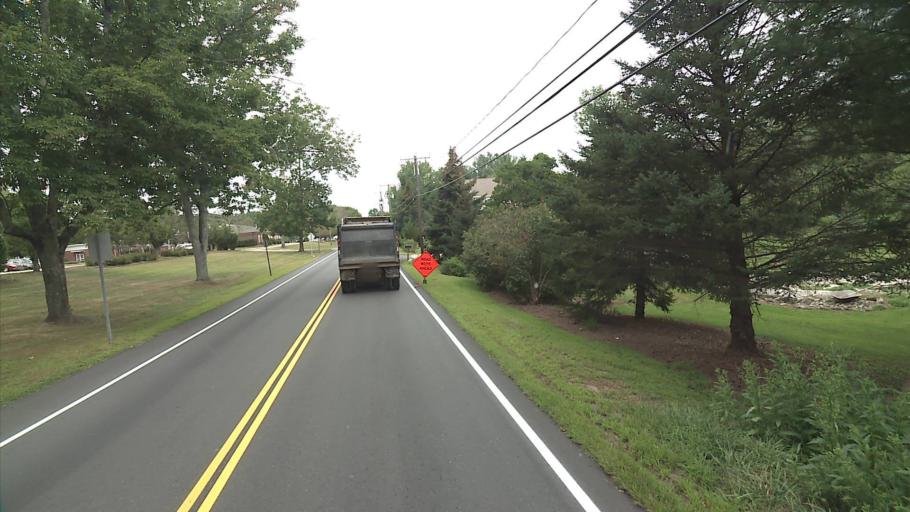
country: US
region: Connecticut
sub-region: Tolland County
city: Hebron
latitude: 41.6511
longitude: -72.3606
